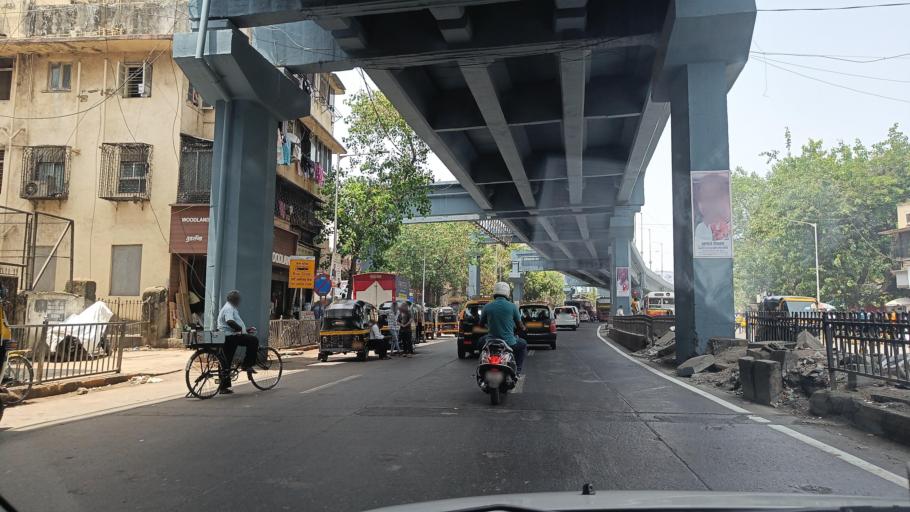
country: IN
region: Maharashtra
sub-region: Mumbai Suburban
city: Mumbai
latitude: 19.0448
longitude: 72.8646
